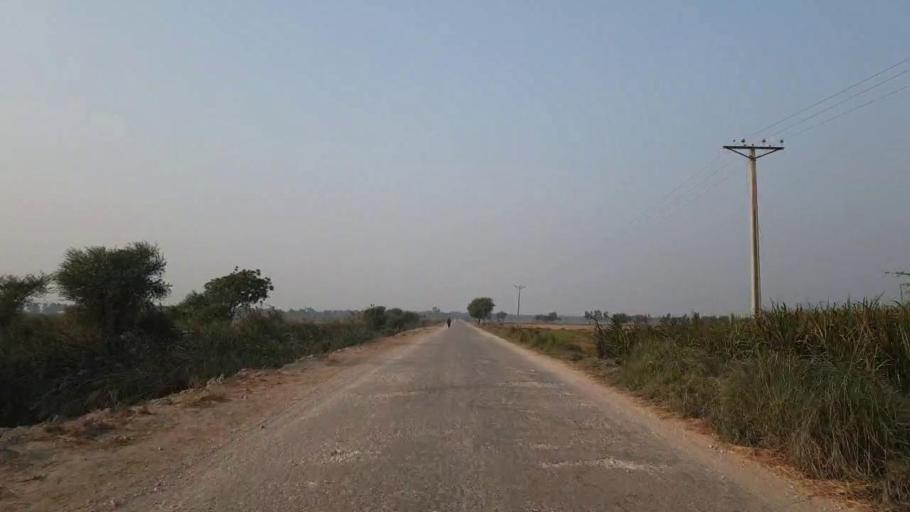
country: PK
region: Sindh
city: Tando Muhammad Khan
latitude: 25.1063
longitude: 68.4303
